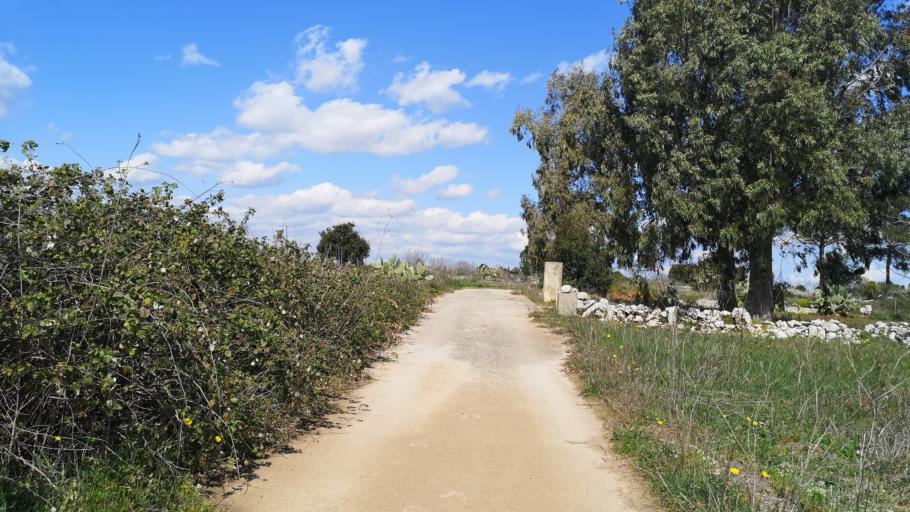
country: IT
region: Apulia
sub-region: Provincia di Lecce
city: Spongano
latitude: 40.0275
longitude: 18.3625
